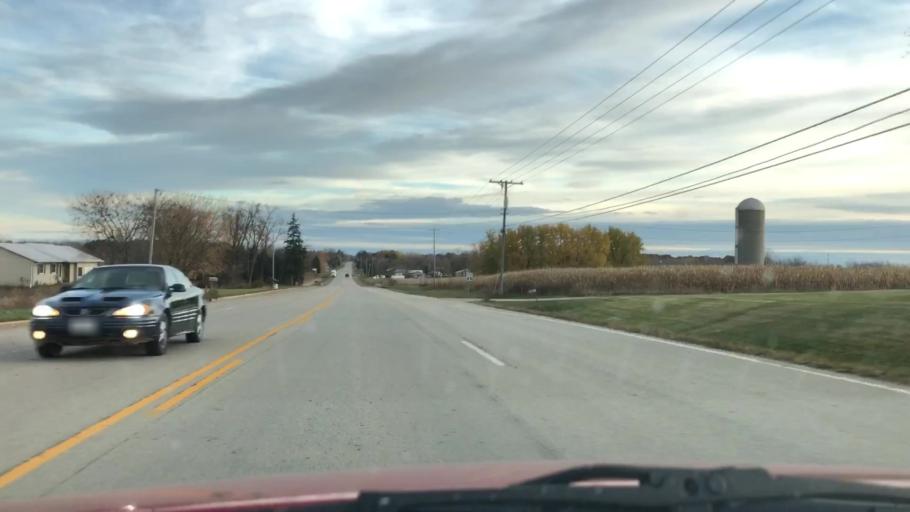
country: US
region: Wisconsin
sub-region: Brown County
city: Oneida
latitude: 44.4339
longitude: -88.2356
